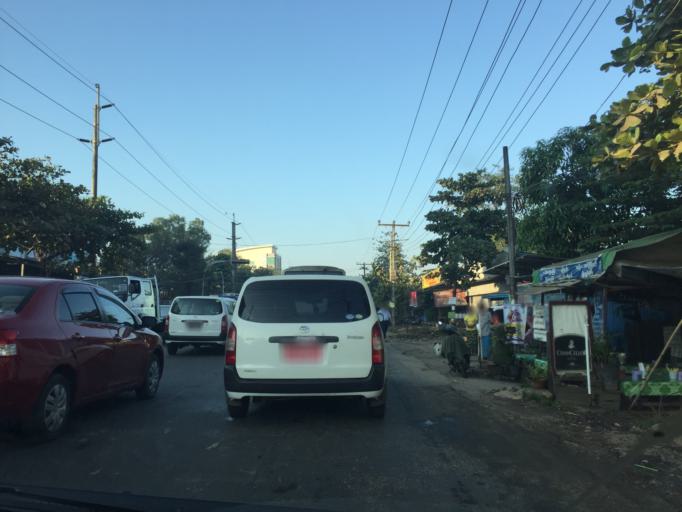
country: MM
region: Yangon
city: Yangon
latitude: 16.8670
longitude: 96.1850
